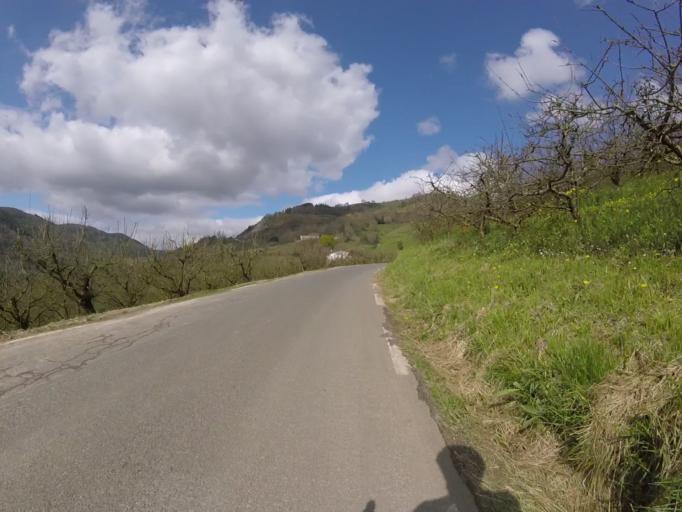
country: ES
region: Basque Country
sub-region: Provincia de Guipuzcoa
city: Tolosa
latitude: 43.1266
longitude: -2.0968
